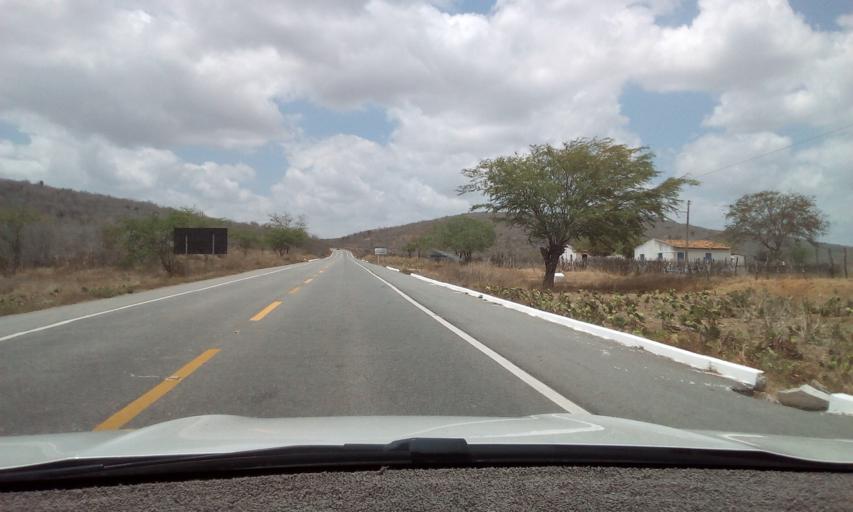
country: BR
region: Paraiba
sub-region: Boqueirao
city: Boqueirao
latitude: -7.6639
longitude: -36.0802
